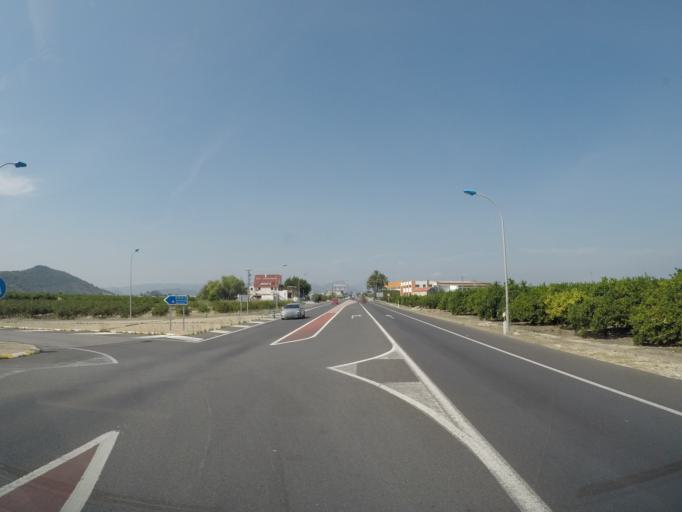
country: ES
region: Valencia
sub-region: Provincia de Valencia
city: Piles
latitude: 38.9293
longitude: -0.1343
